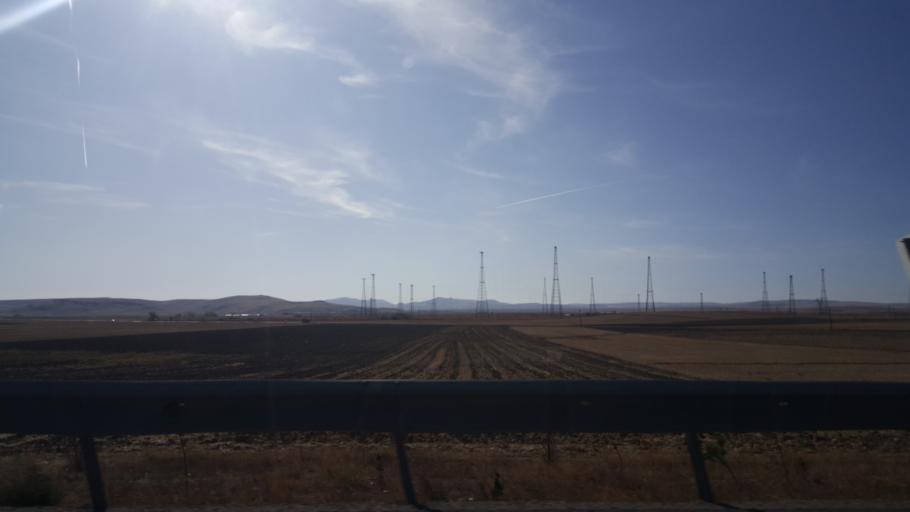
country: TR
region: Ankara
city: Yenice
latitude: 39.4052
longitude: 32.8723
